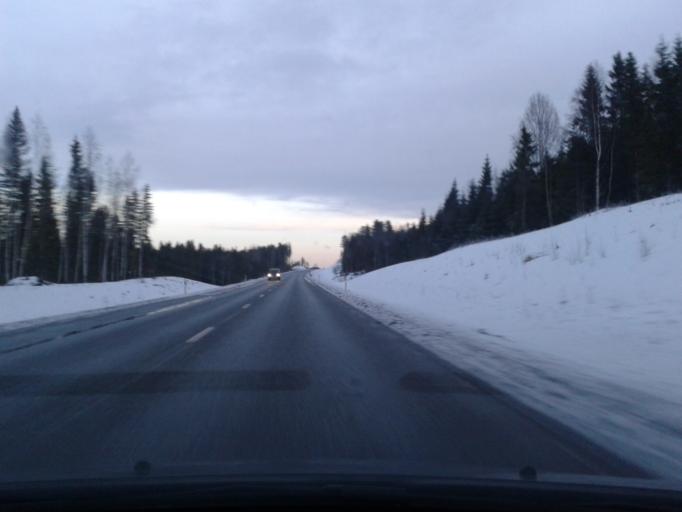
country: SE
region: Vaesternorrland
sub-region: Kramfors Kommun
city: Bollstabruk
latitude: 63.0674
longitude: 17.5801
